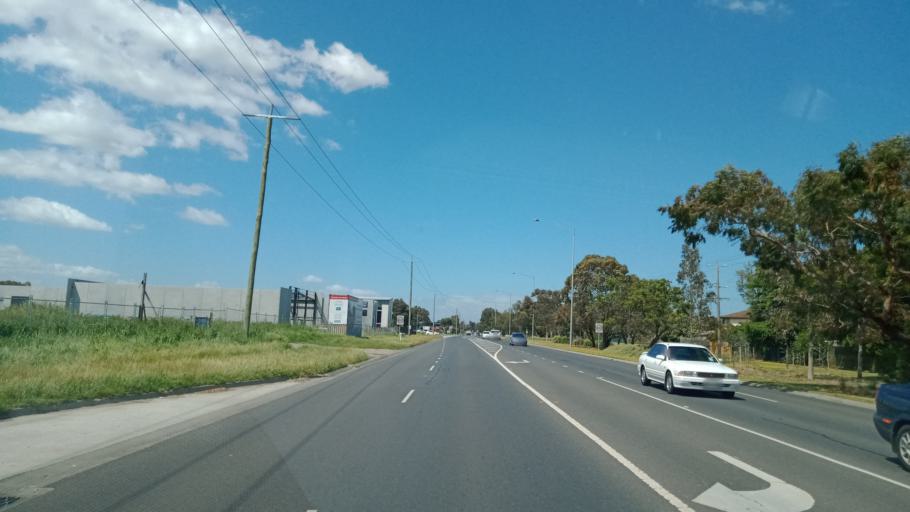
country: AU
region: Victoria
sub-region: Kingston
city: Chelsea Heights
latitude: -38.0339
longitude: 145.1345
